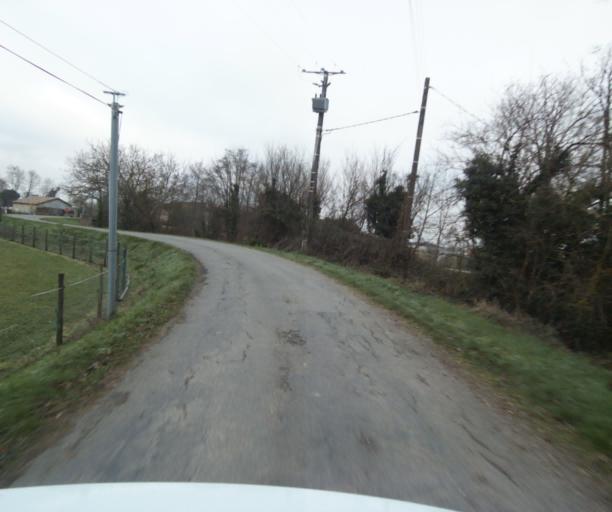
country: FR
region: Midi-Pyrenees
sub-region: Departement du Tarn-et-Garonne
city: Moissac
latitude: 44.1043
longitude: 1.1190
